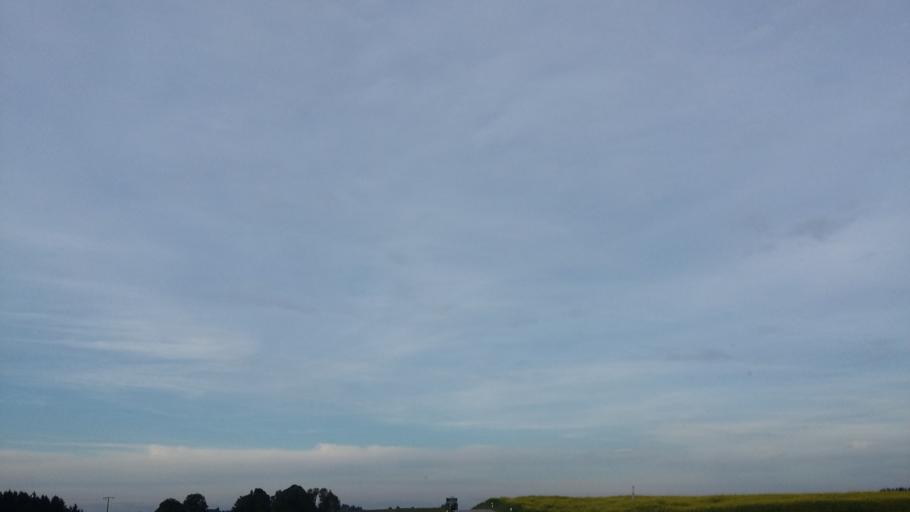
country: DE
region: Bavaria
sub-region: Upper Bavaria
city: Munsing
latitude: 47.8915
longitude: 11.3586
